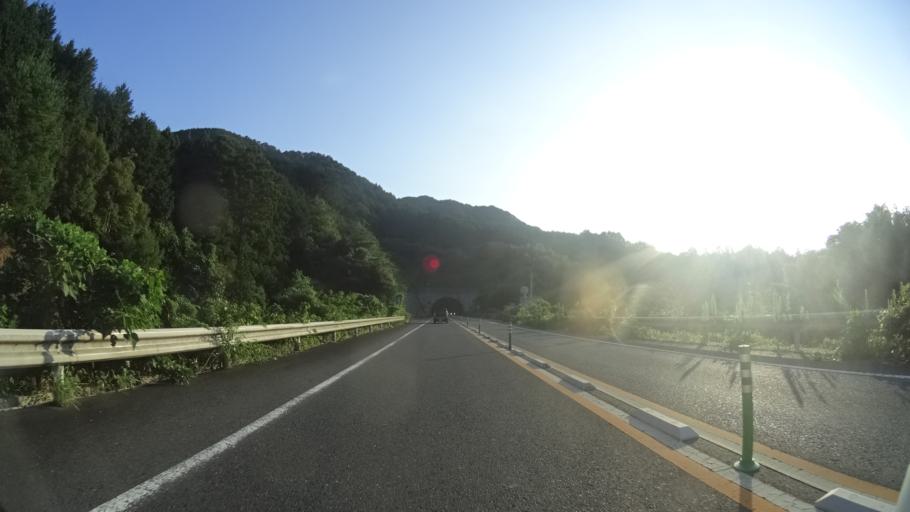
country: JP
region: Yamaguchi
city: Nagato
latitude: 34.3697
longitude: 131.2675
